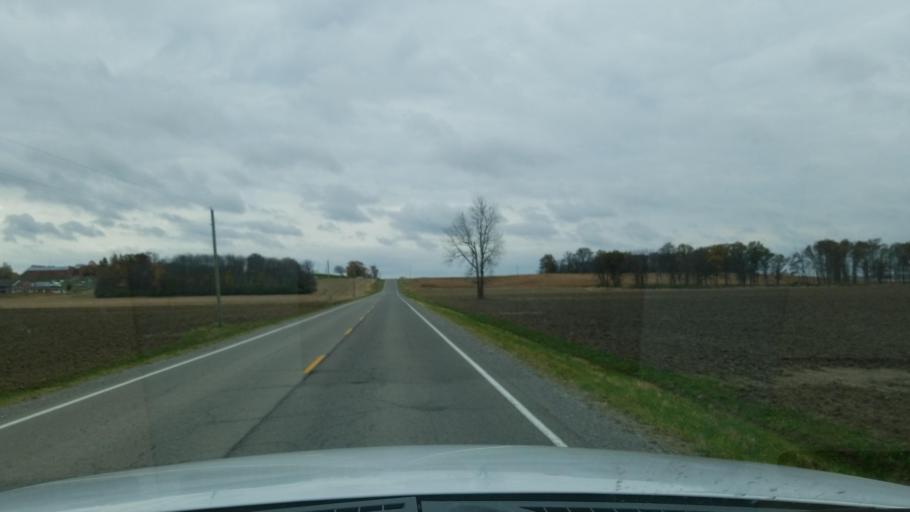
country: US
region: Illinois
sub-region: Saline County
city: Eldorado
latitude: 37.7590
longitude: -88.4383
